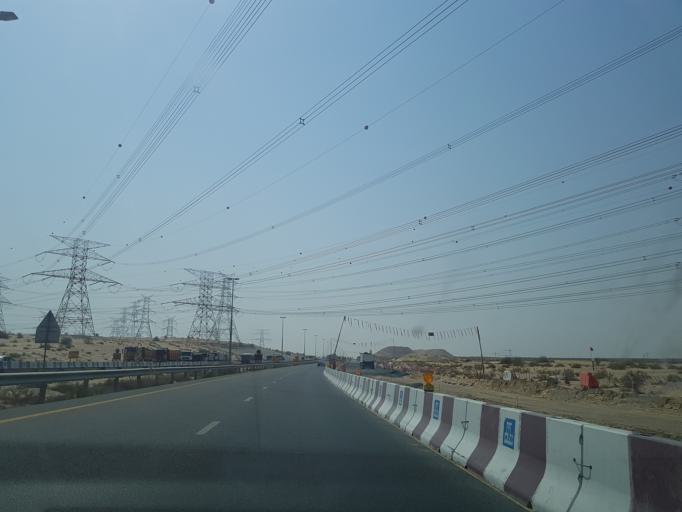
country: AE
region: Ash Shariqah
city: Sharjah
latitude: 25.1481
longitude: 55.4184
